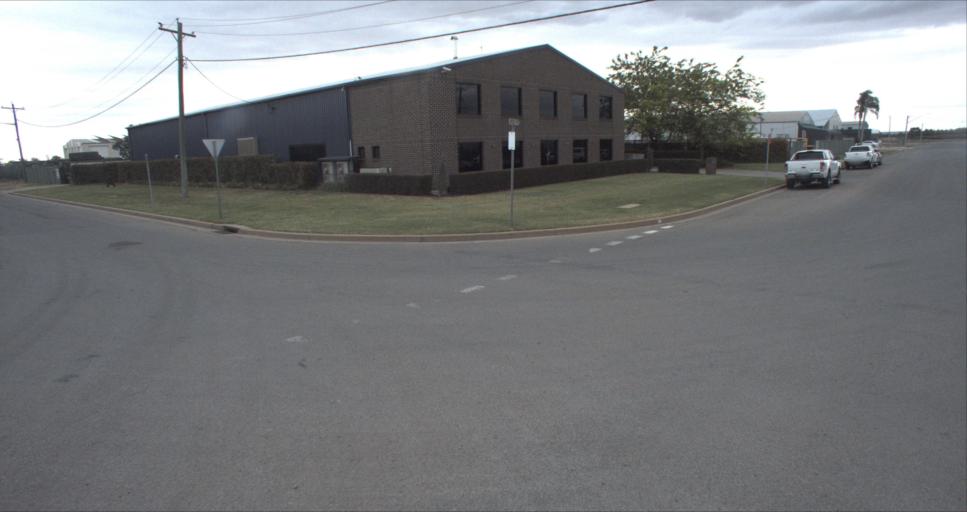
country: AU
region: New South Wales
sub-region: Leeton
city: Leeton
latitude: -34.5487
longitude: 146.3906
